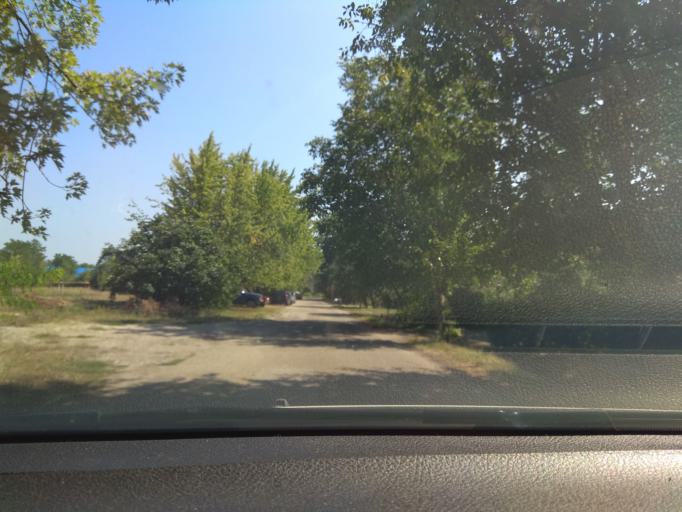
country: HU
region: Borsod-Abauj-Zemplen
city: Miskolc
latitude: 48.0763
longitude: 20.7891
